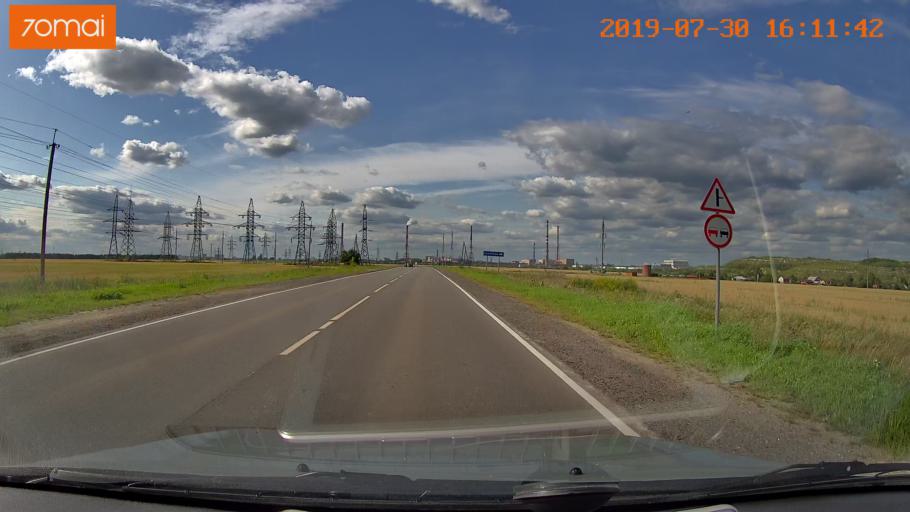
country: RU
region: Moskovskaya
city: Lopatinskiy
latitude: 55.2801
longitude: 38.7079
